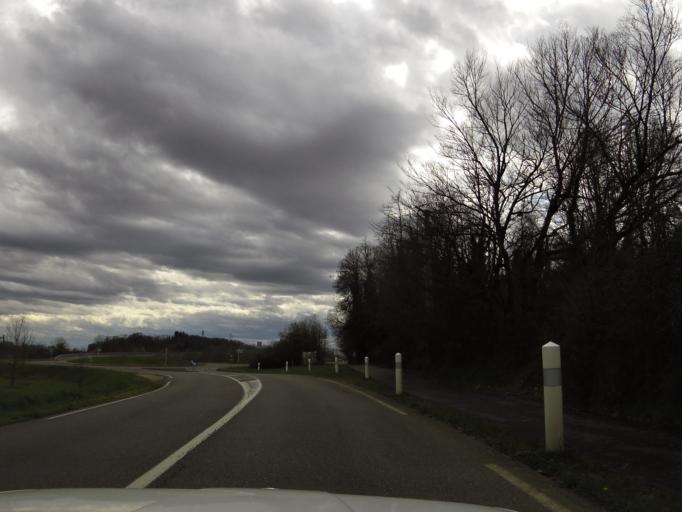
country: FR
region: Rhone-Alpes
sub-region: Departement de l'Ain
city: Meximieux
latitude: 45.9124
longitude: 5.2162
